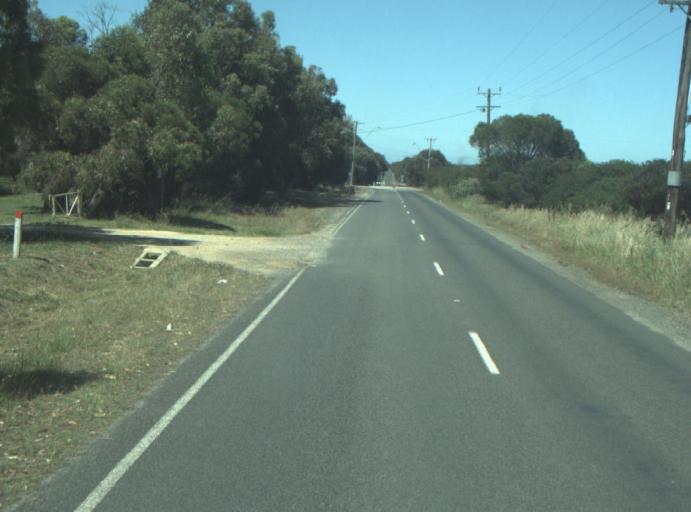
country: AU
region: Victoria
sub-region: Greater Geelong
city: Breakwater
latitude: -38.2198
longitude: 144.3568
